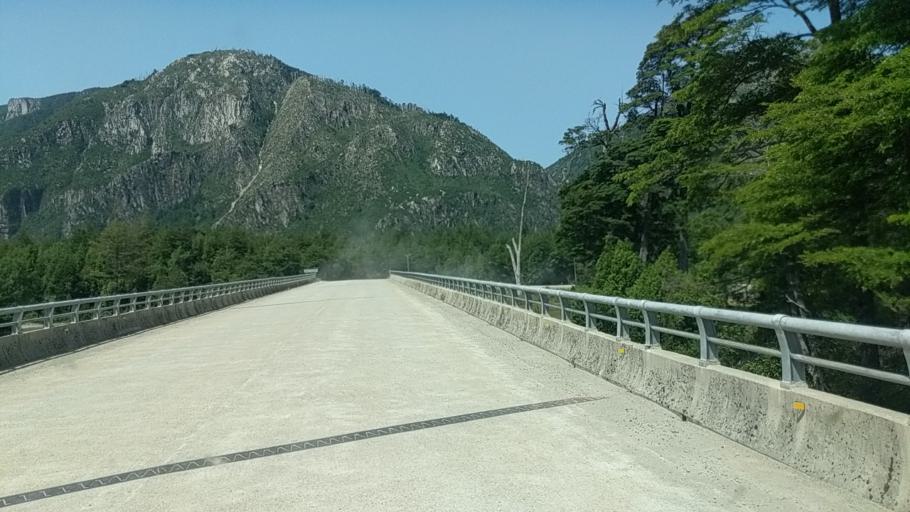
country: CL
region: Los Lagos
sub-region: Provincia de Palena
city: Palena
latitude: -43.4808
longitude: -72.1297
